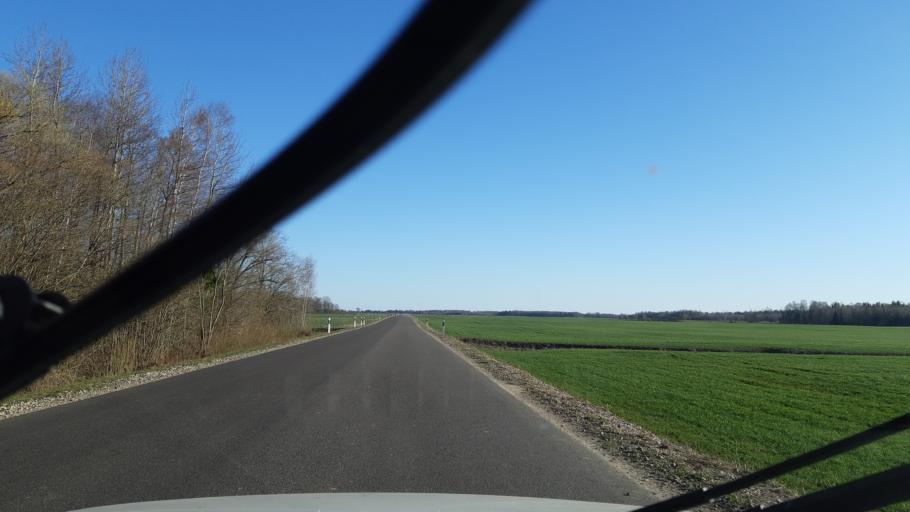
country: LT
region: Kauno apskritis
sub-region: Kaunas
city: Sargenai
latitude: 55.0287
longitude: 23.7601
